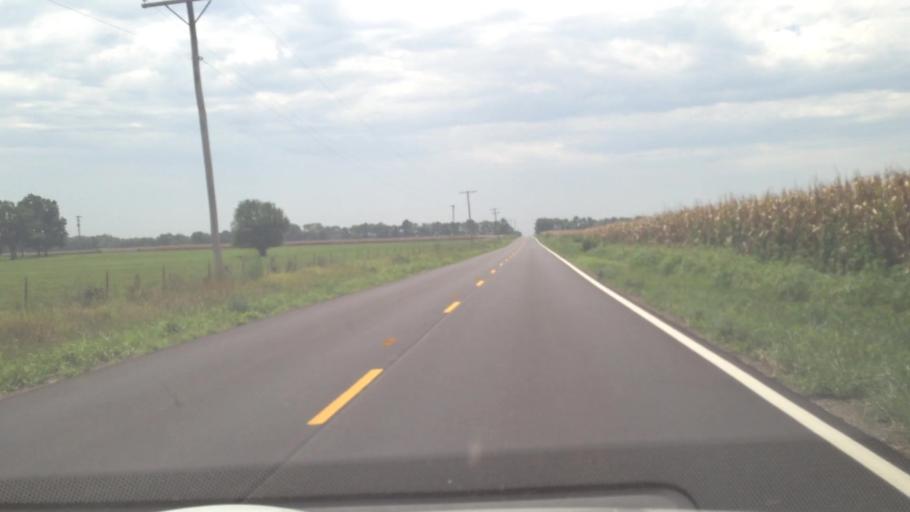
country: US
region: Kansas
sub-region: Crawford County
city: Girard
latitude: 37.6446
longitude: -94.9698
